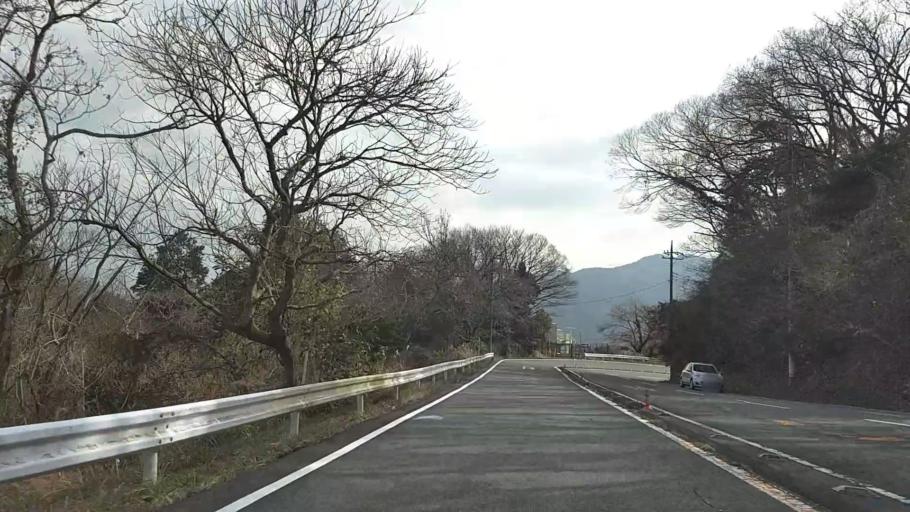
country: JP
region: Shizuoka
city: Ito
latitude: 35.0208
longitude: 139.0651
